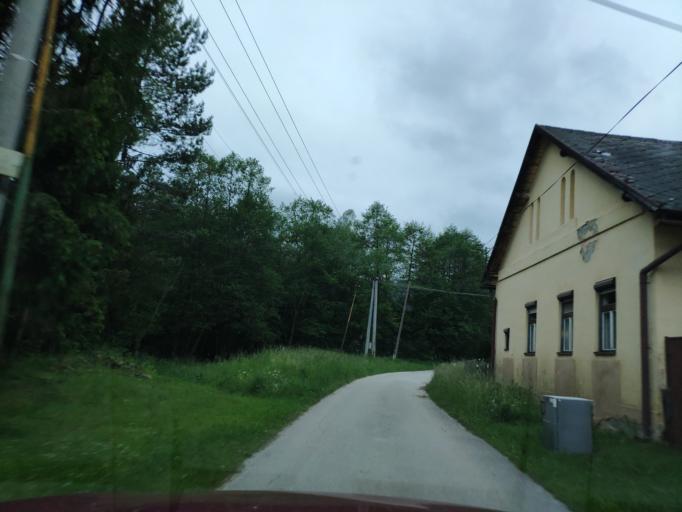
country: SK
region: Kosicky
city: Medzev
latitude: 48.7291
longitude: 20.7258
